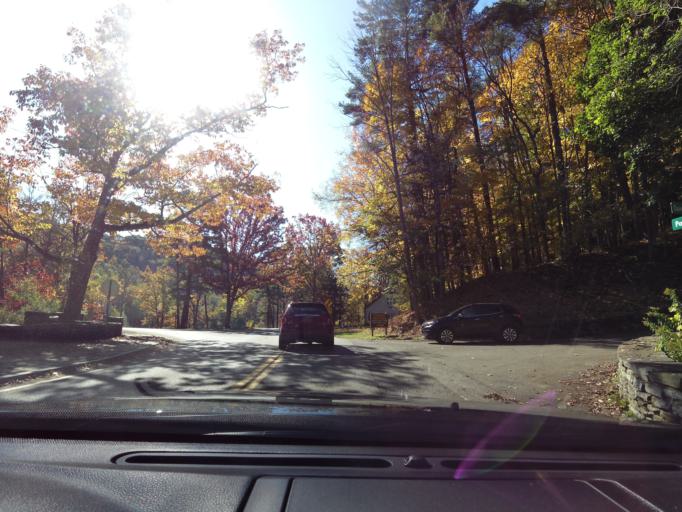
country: US
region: New York
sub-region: Wyoming County
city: Castile
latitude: 42.5857
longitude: -78.0408
